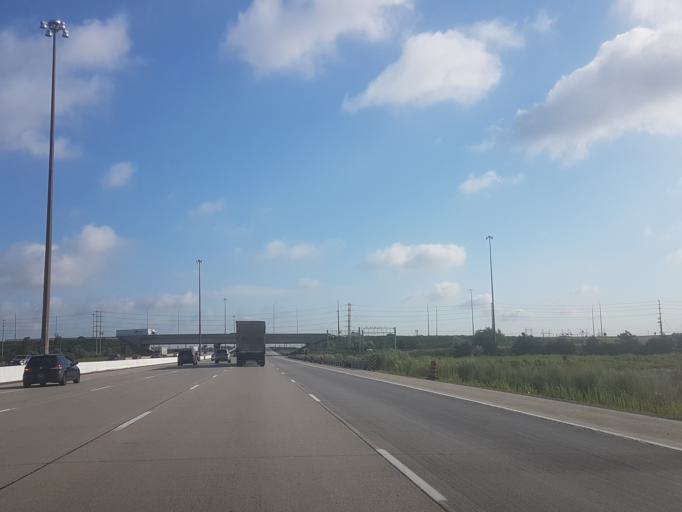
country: CA
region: Ontario
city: Brampton
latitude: 43.6971
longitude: -79.6851
